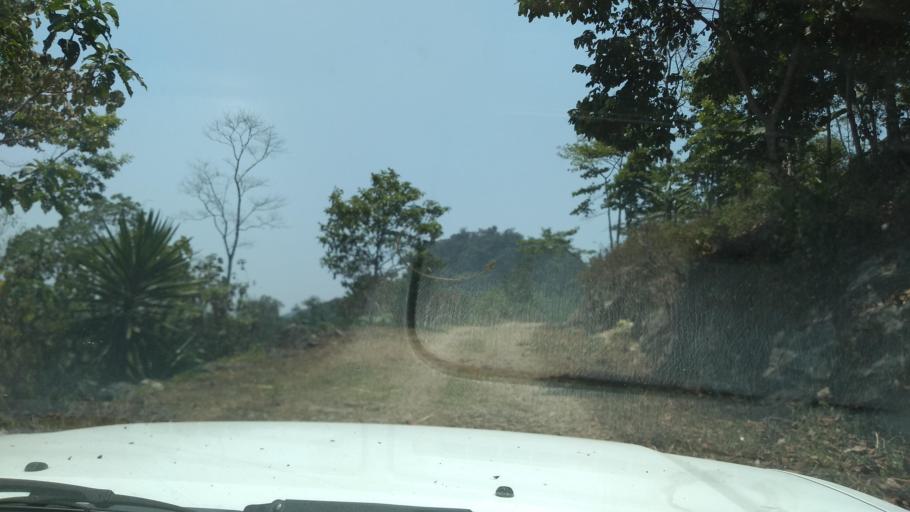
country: MX
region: Veracruz
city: Motzorongo
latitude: 18.6157
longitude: -96.7598
